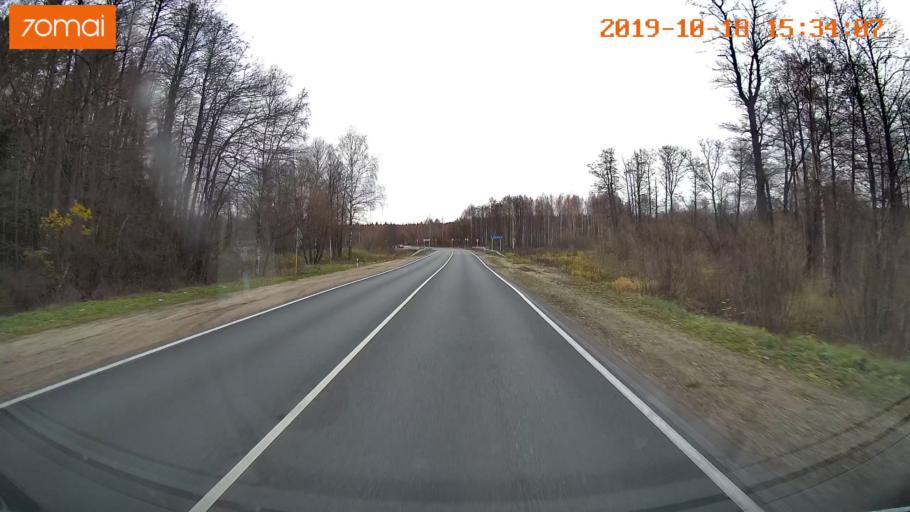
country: RU
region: Vladimir
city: Anopino
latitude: 55.8508
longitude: 40.6450
